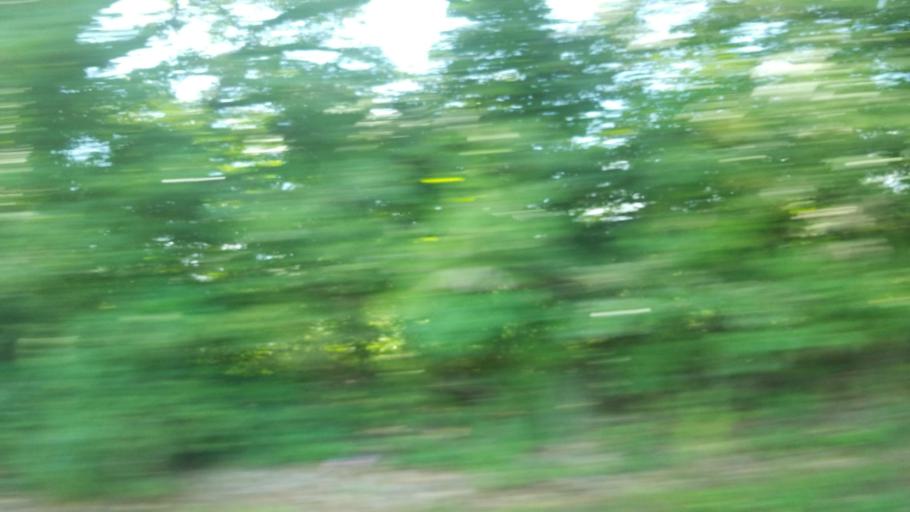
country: US
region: Illinois
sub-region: Williamson County
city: Johnston City
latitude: 37.7850
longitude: -88.8175
